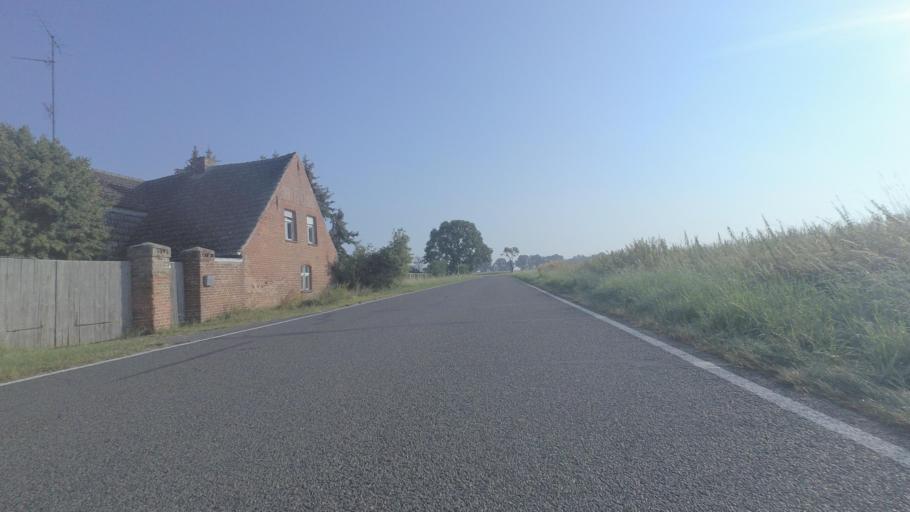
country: DE
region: Brandenburg
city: Heiligengrabe
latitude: 53.2642
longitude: 12.3350
